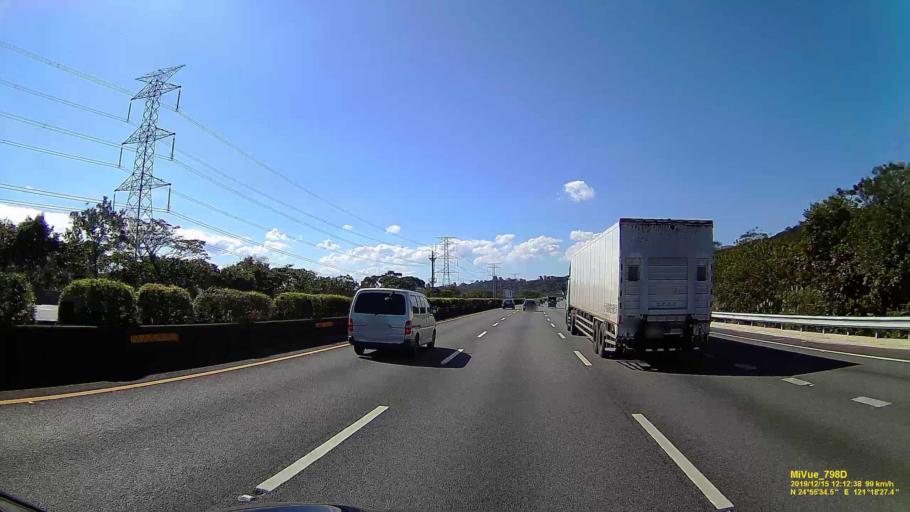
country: TW
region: Taiwan
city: Daxi
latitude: 24.9265
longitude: 121.3069
